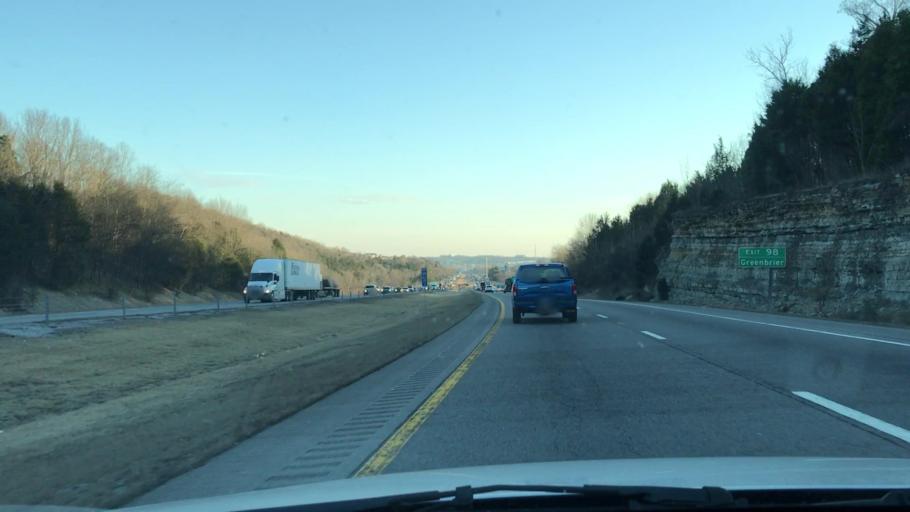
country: US
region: Tennessee
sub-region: Sumner County
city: Millersville
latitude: 36.3536
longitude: -86.7198
